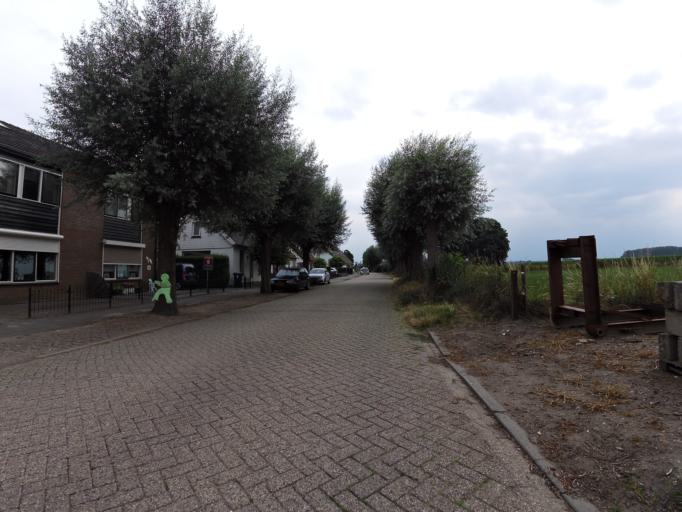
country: NL
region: Gelderland
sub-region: Gemeente Zevenaar
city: Zevenaar
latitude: 51.8637
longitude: 6.0391
